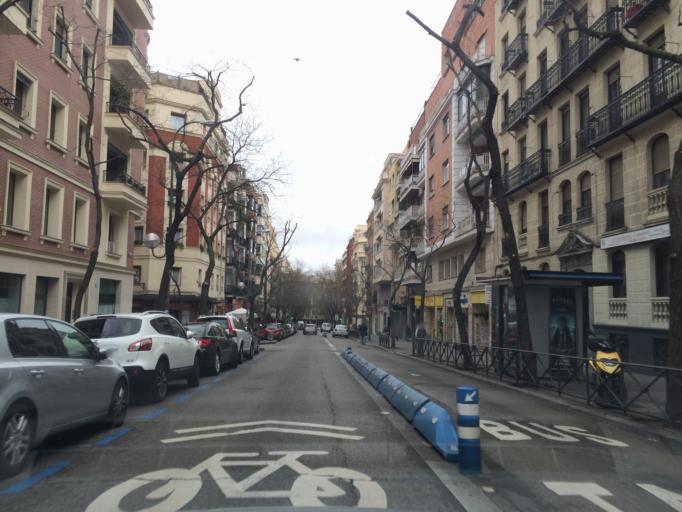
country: ES
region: Madrid
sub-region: Provincia de Madrid
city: Chamberi
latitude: 40.4329
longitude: -3.7133
